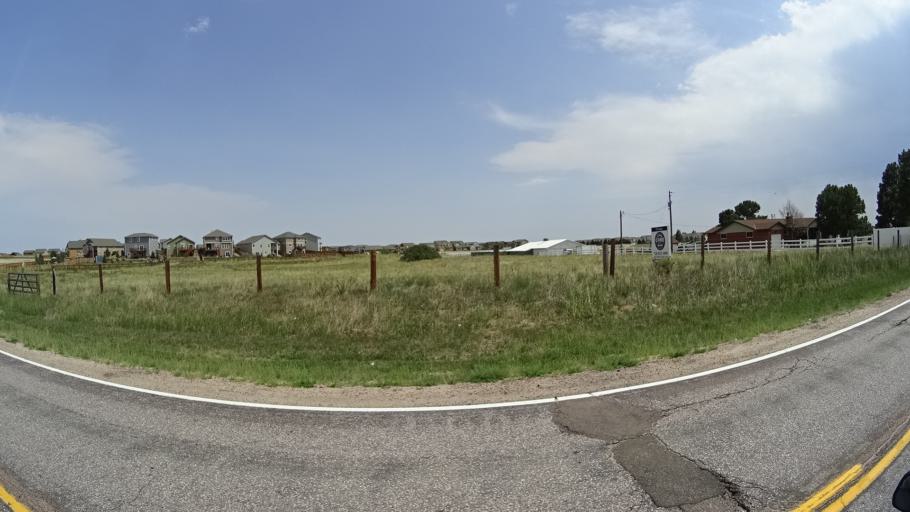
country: US
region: Colorado
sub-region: El Paso County
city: Cimarron Hills
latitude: 38.9290
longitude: -104.7147
